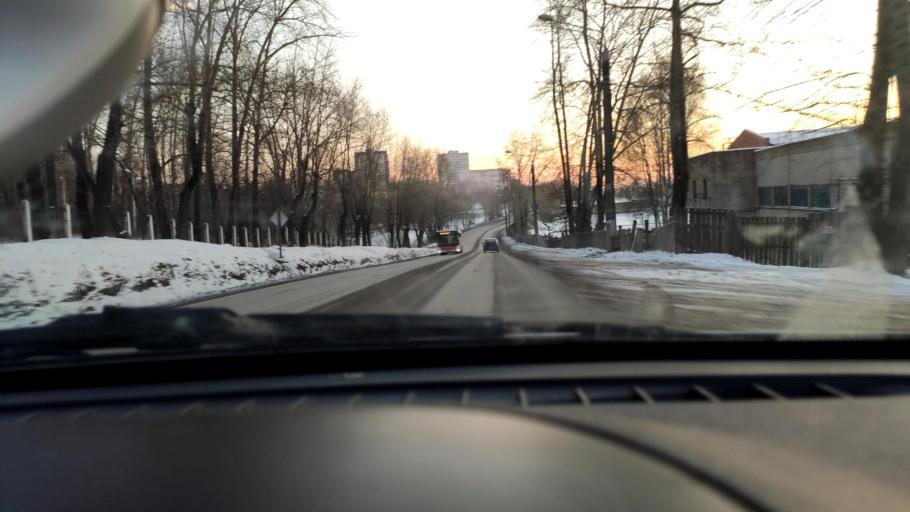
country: RU
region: Perm
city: Perm
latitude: 58.1184
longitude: 56.3684
